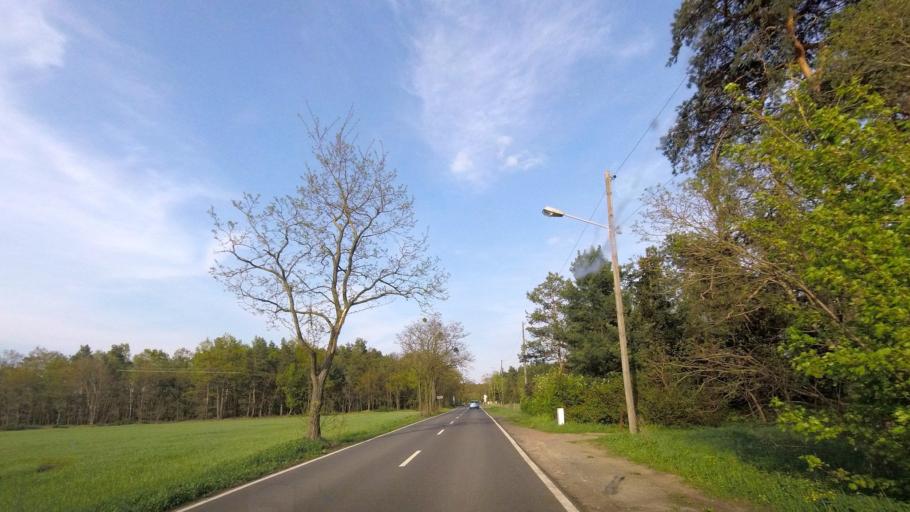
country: DE
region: Saxony-Anhalt
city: Abtsdorf
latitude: 51.8778
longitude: 12.7095
